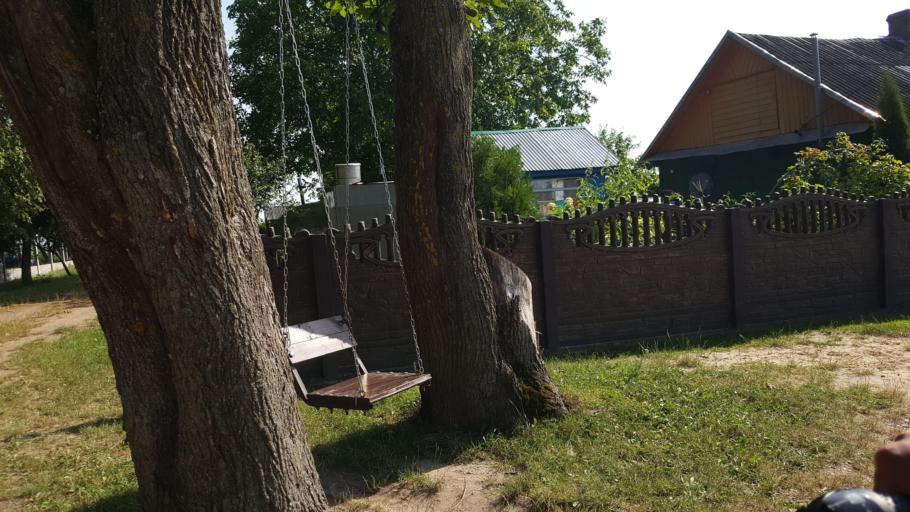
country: BY
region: Brest
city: Zhabinka
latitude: 52.2379
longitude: 24.0152
